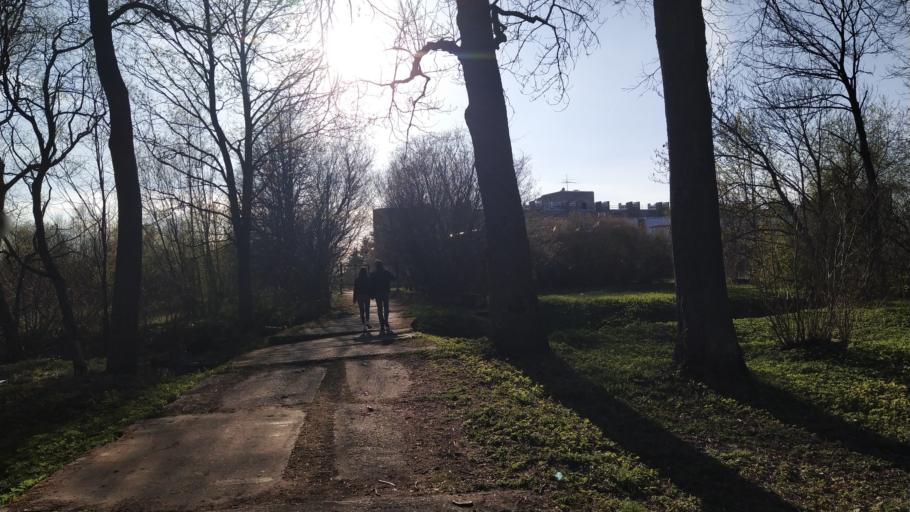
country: RU
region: St.-Petersburg
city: Aleksandrovskaya
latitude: 59.7090
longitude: 30.3426
